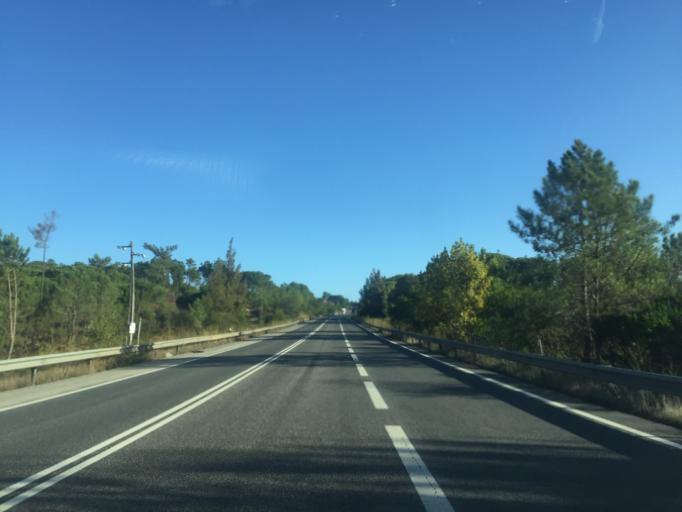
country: PT
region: Lisbon
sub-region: Azambuja
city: Alcoentre
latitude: 39.2664
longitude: -8.9465
